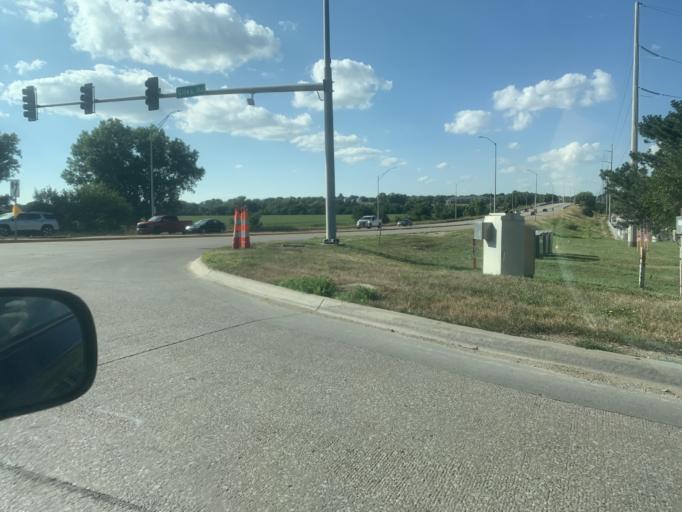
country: US
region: Nebraska
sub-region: Sarpy County
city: Chalco
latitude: 41.1764
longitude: -96.1386
